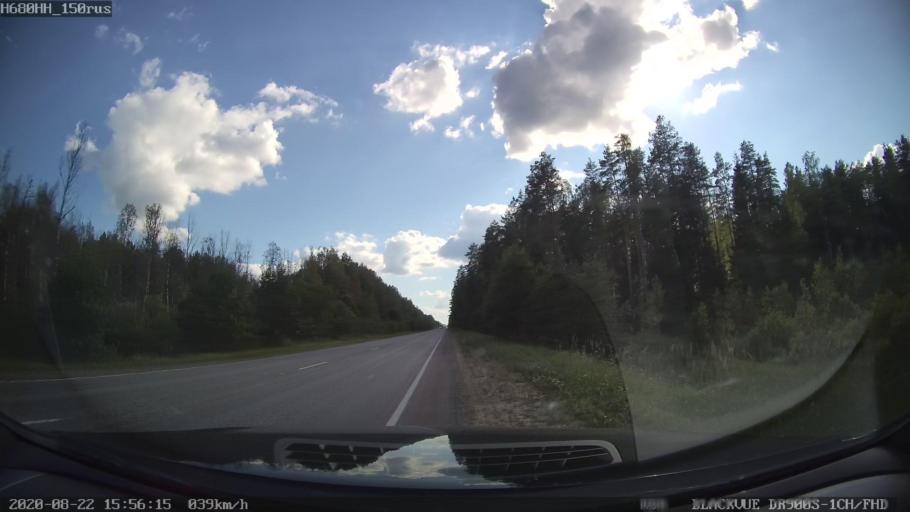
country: RU
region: Tverskaya
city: Bezhetsk
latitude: 57.6116
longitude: 36.3646
